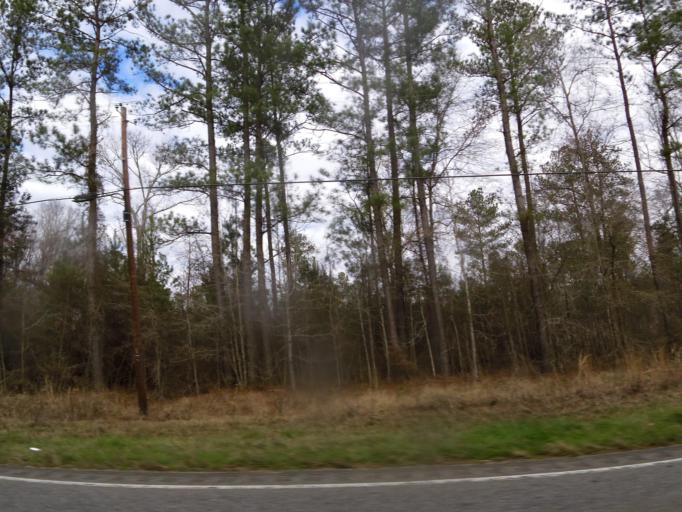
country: US
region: Alabama
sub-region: Barbour County
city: Eufaula
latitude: 31.9568
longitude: -85.2042
